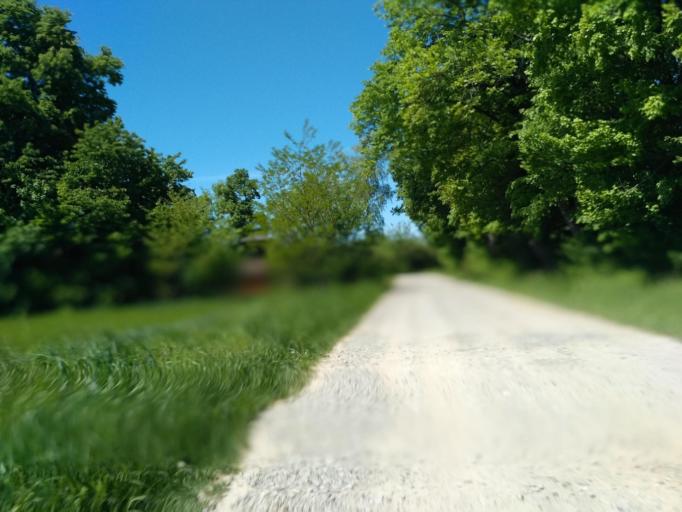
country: PL
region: Subcarpathian Voivodeship
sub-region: Powiat sanocki
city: Dlugie
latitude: 49.6060
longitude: 22.0362
